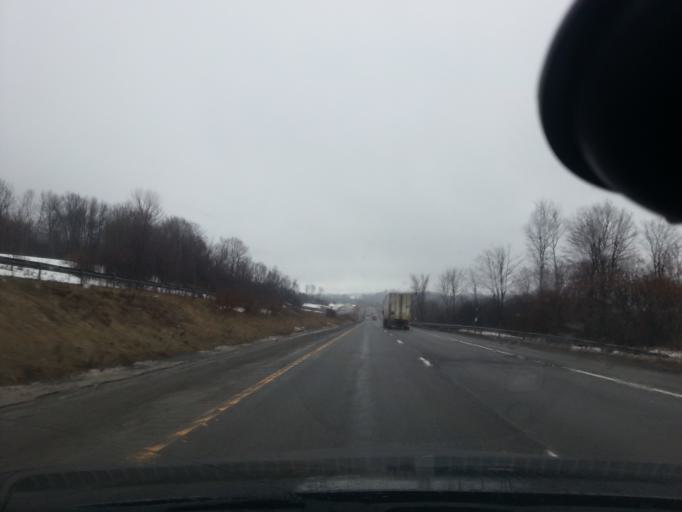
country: US
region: New York
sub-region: Onondaga County
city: Nedrow
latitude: 42.8278
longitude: -76.1246
